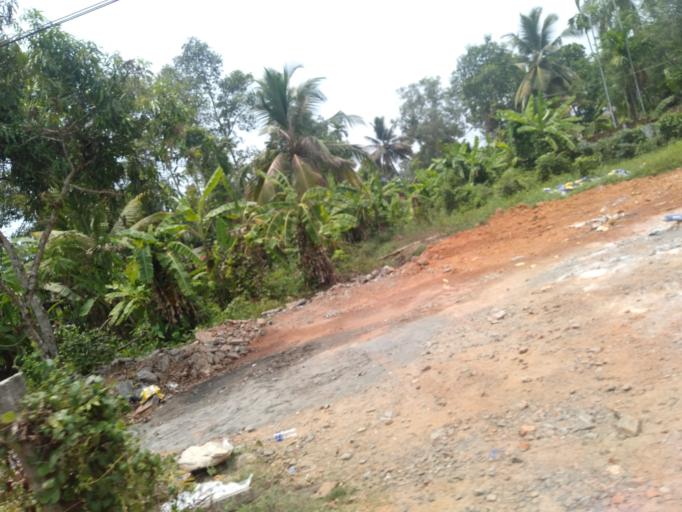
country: IN
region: Kerala
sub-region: Alappuzha
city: Alleppey
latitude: 9.4039
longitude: 76.4101
